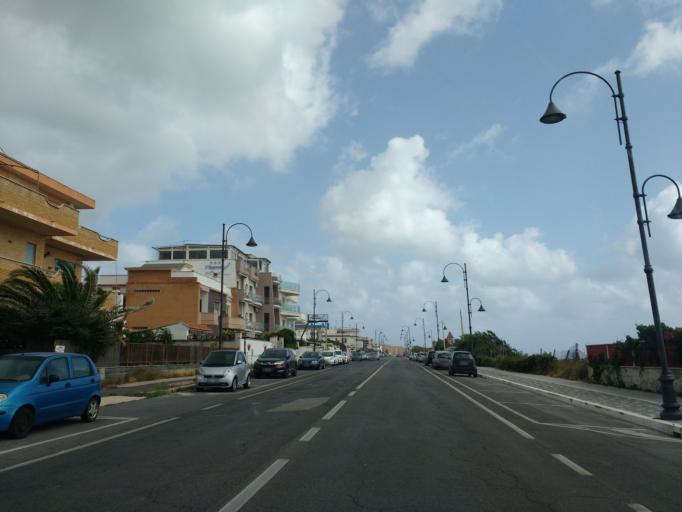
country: IT
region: Latium
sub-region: Citta metropolitana di Roma Capitale
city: Anzio
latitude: 41.4600
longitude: 12.6134
